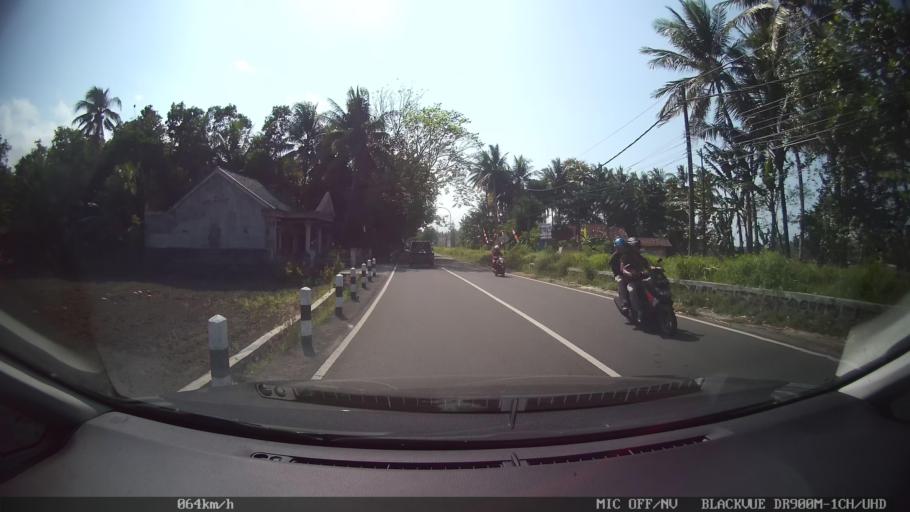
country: ID
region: Daerah Istimewa Yogyakarta
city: Srandakan
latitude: -7.9300
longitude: 110.1924
